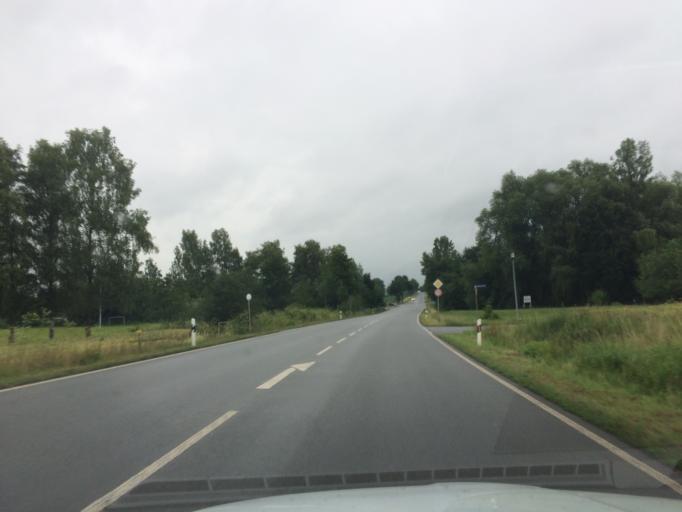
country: DE
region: Hesse
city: Trendelburg
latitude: 51.5376
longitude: 9.4104
